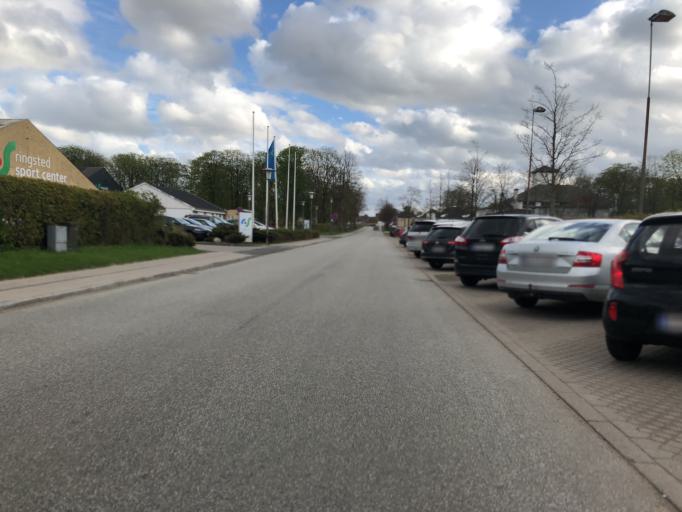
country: DK
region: Zealand
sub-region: Ringsted Kommune
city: Ringsted
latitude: 55.4481
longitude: 11.7997
